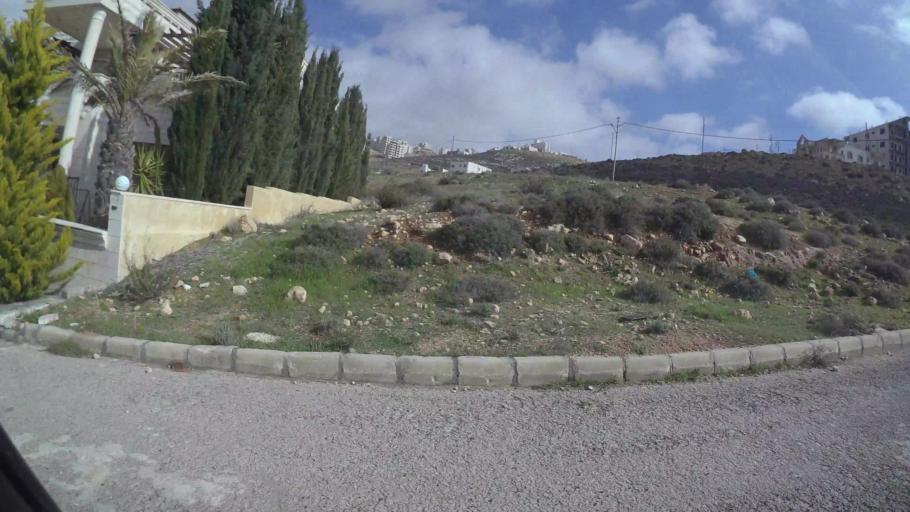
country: JO
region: Amman
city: Al Jubayhah
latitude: 32.0597
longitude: 35.8616
